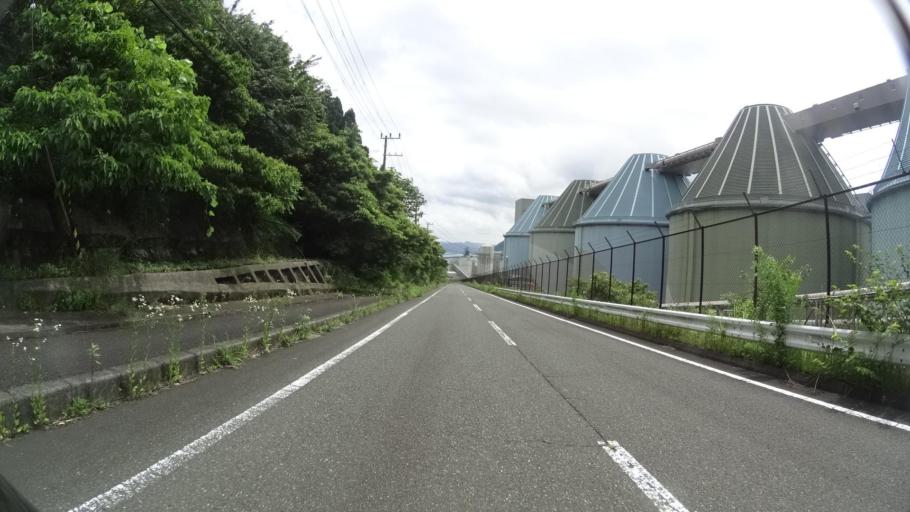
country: JP
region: Kyoto
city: Maizuru
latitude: 35.5279
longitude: 135.3452
